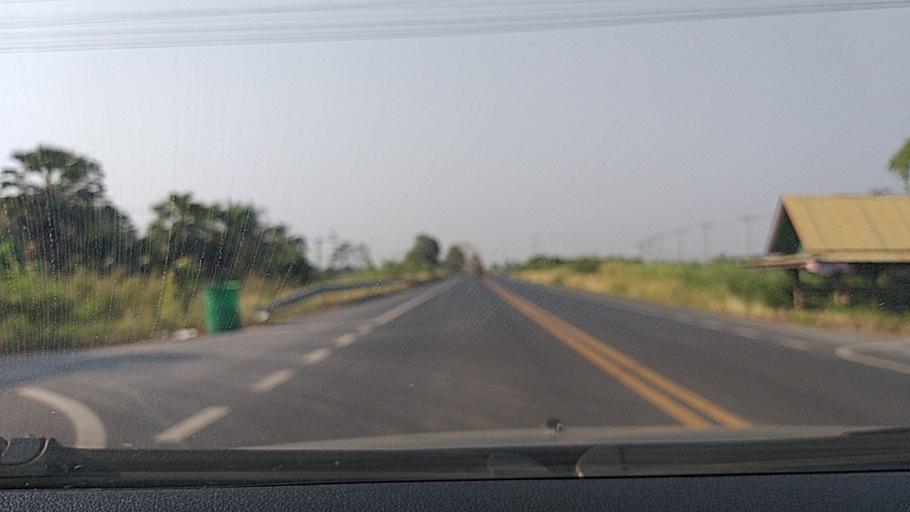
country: TH
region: Sing Buri
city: Phrom Buri
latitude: 14.8040
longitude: 100.4345
